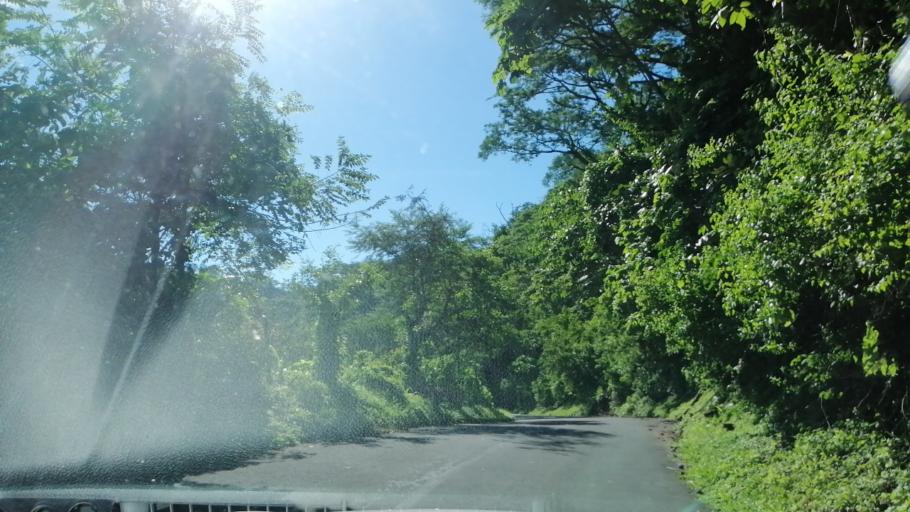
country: SV
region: Morazan
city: Cacaopera
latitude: 13.7865
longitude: -88.0318
